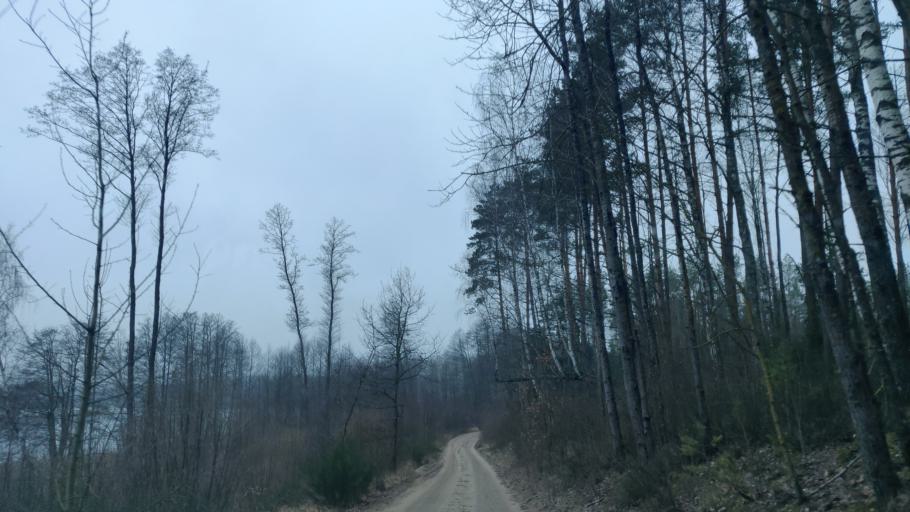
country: LT
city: Trakai
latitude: 54.5527
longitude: 24.9430
